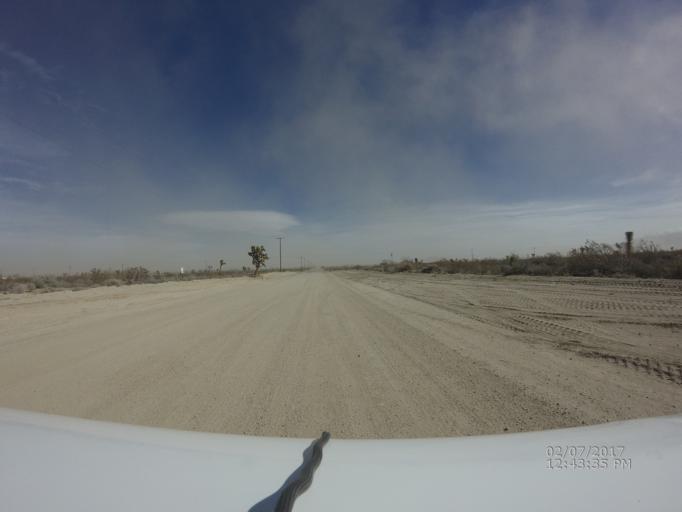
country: US
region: California
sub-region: Los Angeles County
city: Lake Los Angeles
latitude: 34.5873
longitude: -117.8116
